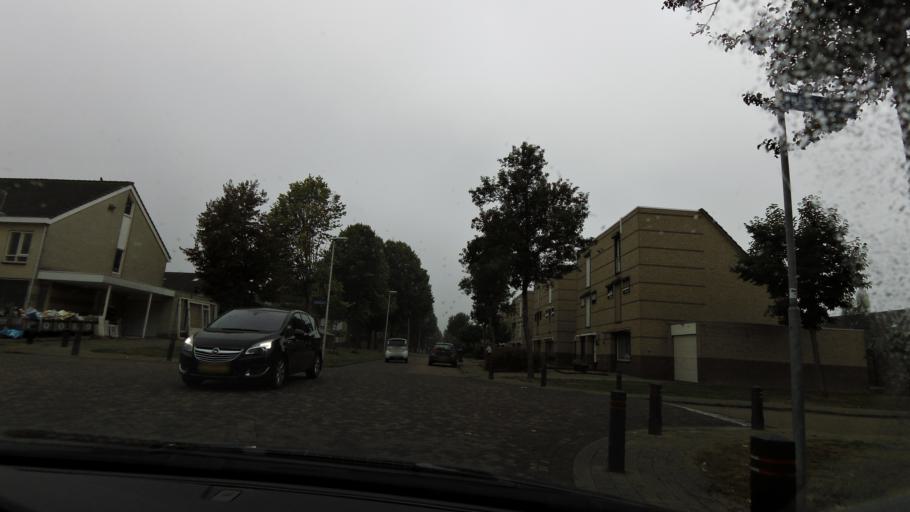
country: NL
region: Limburg
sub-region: Gemeente Heerlen
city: Nieuw-Lotbroek
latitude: 50.9039
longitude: 5.9535
